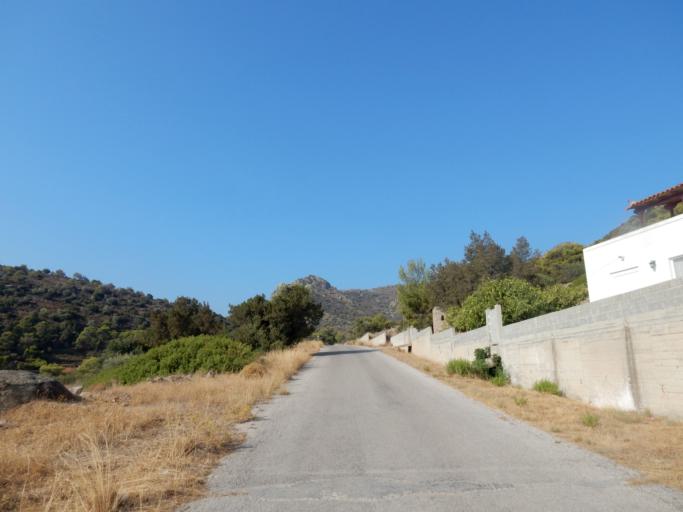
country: GR
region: Attica
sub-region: Nomos Piraios
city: Vathi
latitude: 37.7095
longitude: 23.5195
